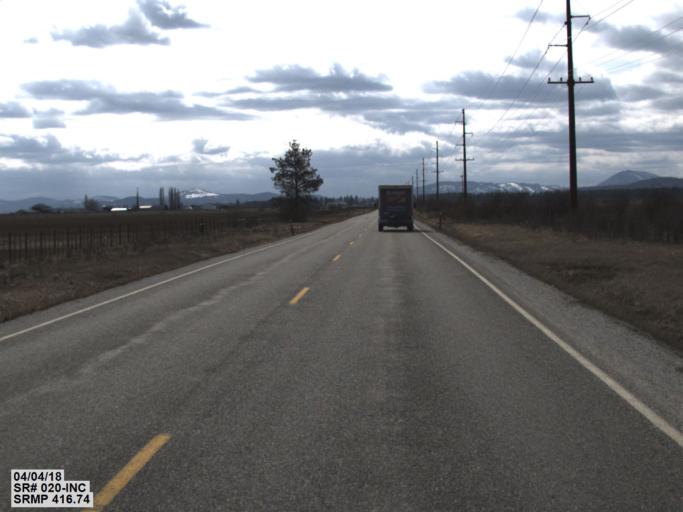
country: US
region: Washington
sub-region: Pend Oreille County
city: Newport
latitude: 48.3705
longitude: -117.3047
